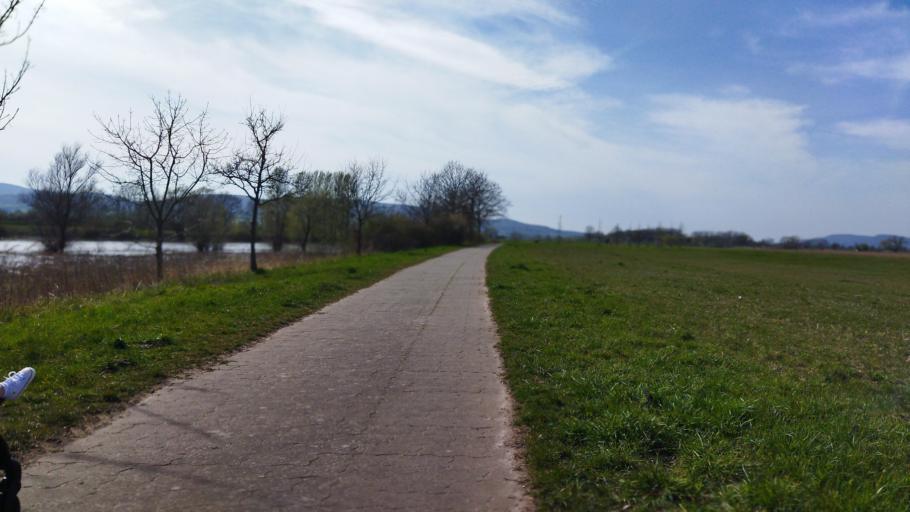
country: DE
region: Lower Saxony
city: Hessisch Oldendorf
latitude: 52.1592
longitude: 9.2476
